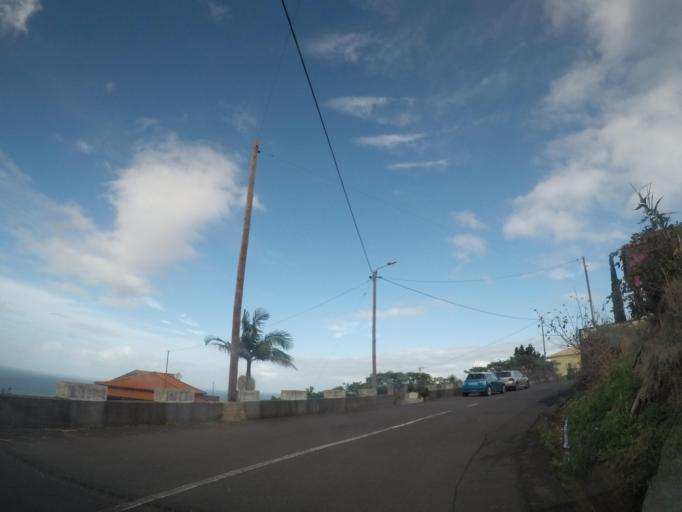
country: PT
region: Madeira
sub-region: Santana
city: Santana
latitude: 32.7896
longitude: -16.8484
